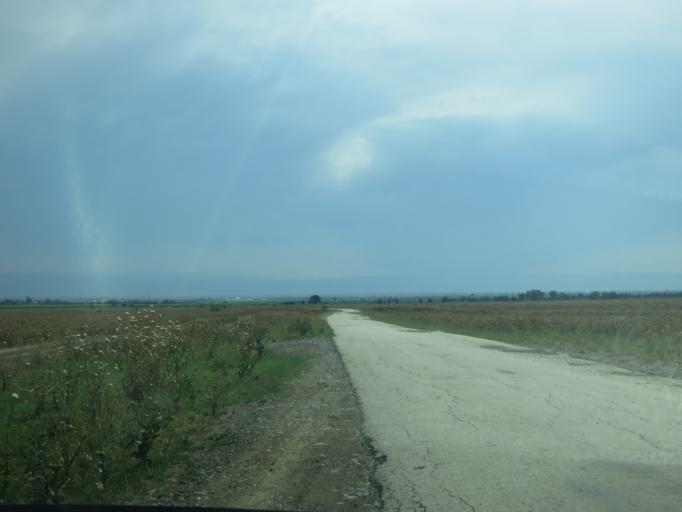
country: GE
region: Kvemo Kartli
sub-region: Gardabani
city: Gardabani
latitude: 41.4830
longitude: 45.1787
